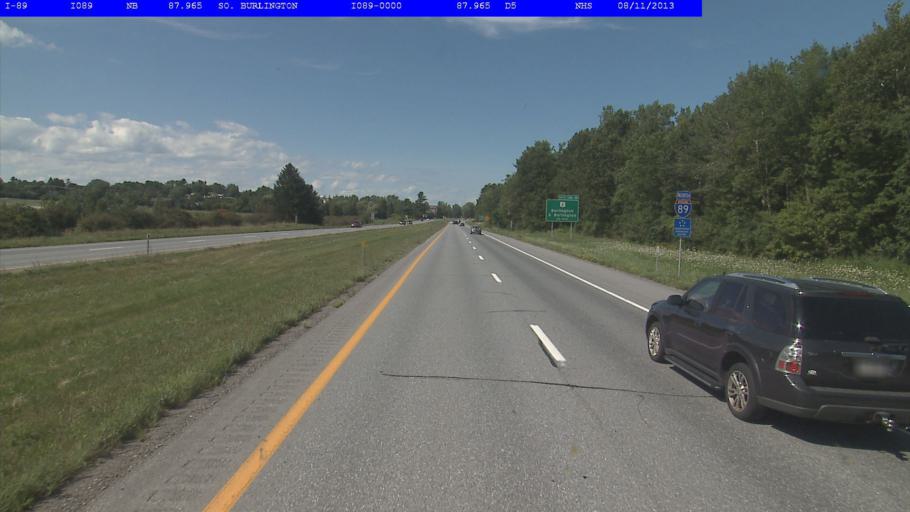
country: US
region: Vermont
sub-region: Chittenden County
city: South Burlington
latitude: 44.4591
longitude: -73.1847
